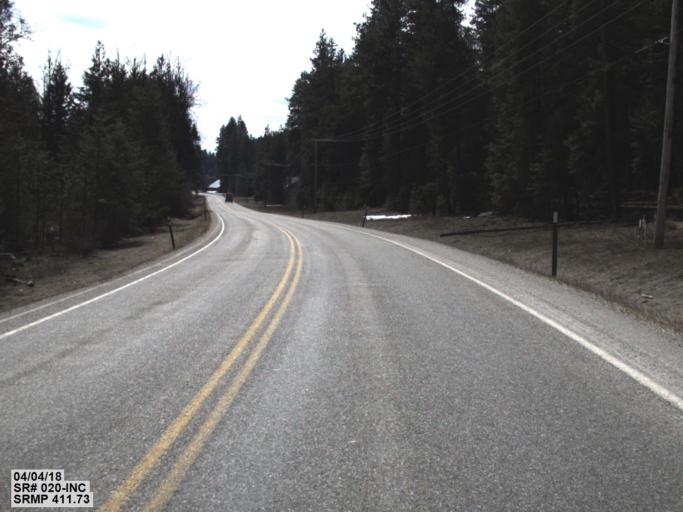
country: US
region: Washington
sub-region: Pend Oreille County
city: Newport
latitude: 48.4392
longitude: -117.3237
